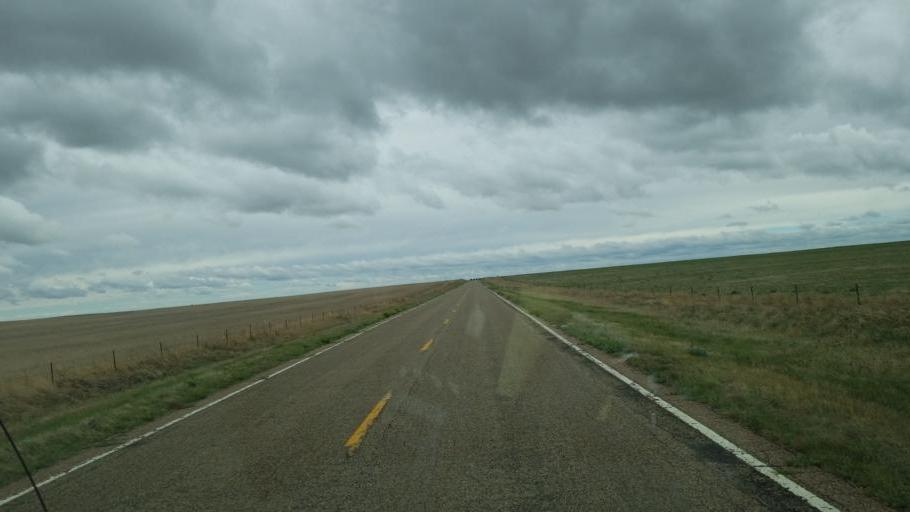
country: US
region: Colorado
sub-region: Lincoln County
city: Hugo
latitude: 38.8516
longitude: -103.6517
